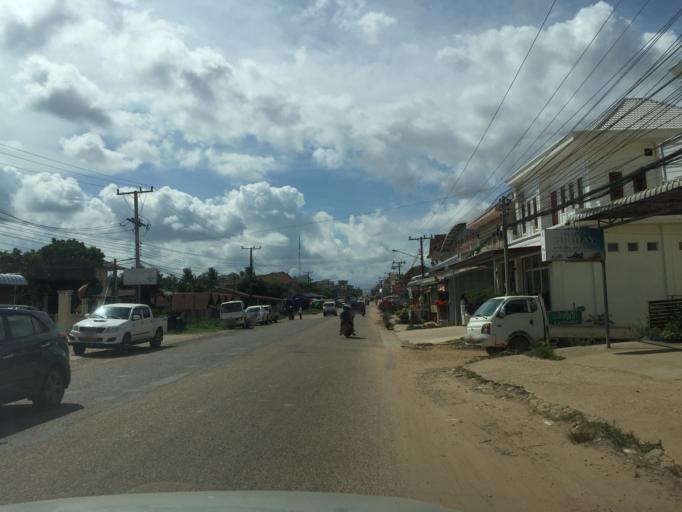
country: LA
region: Savannahkhet
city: Savannakhet
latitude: 16.5483
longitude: 104.7512
